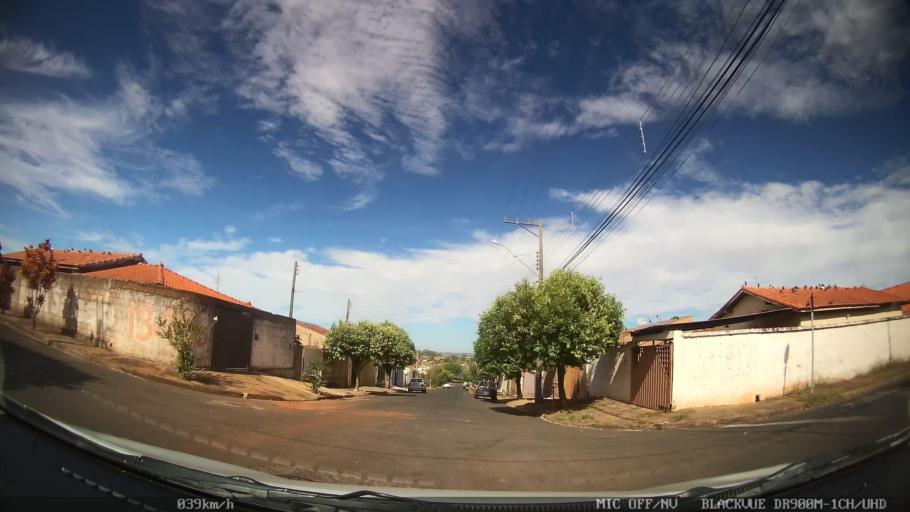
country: BR
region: Sao Paulo
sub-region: Catanduva
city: Catanduva
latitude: -21.1234
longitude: -48.9396
